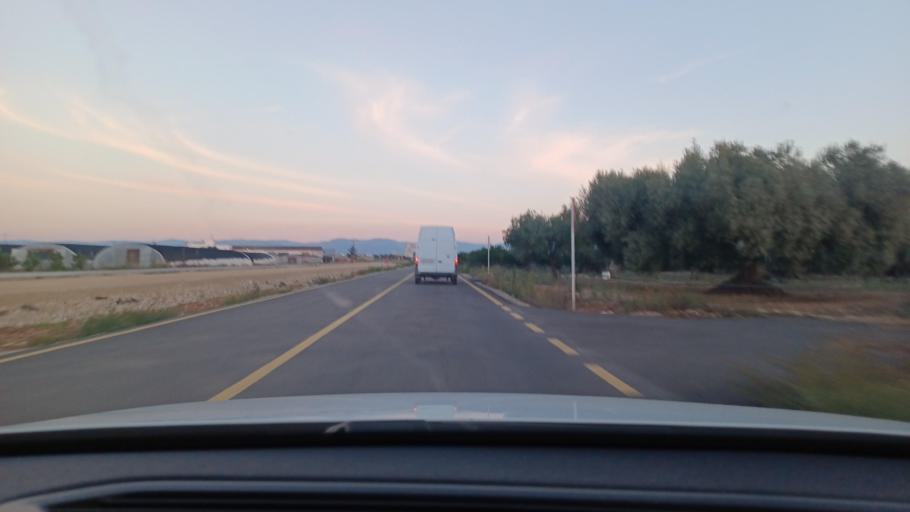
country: ES
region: Catalonia
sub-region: Provincia de Tarragona
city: Alcanar
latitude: 40.5396
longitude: 0.4398
